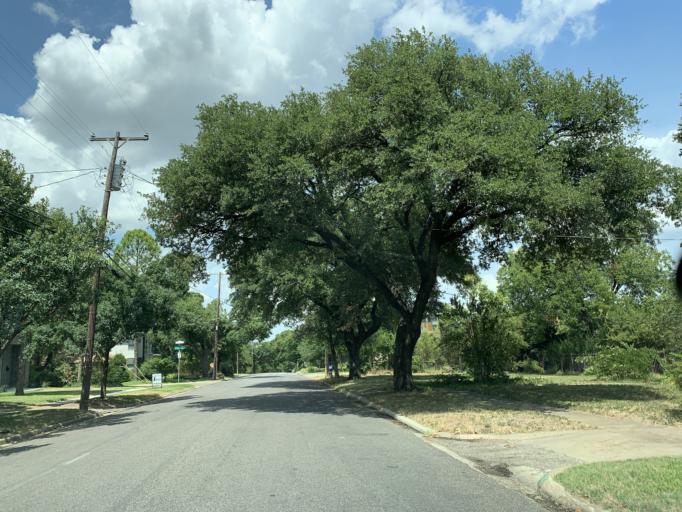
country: US
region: Texas
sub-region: Dallas County
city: Cockrell Hill
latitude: 32.7518
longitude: -96.8546
